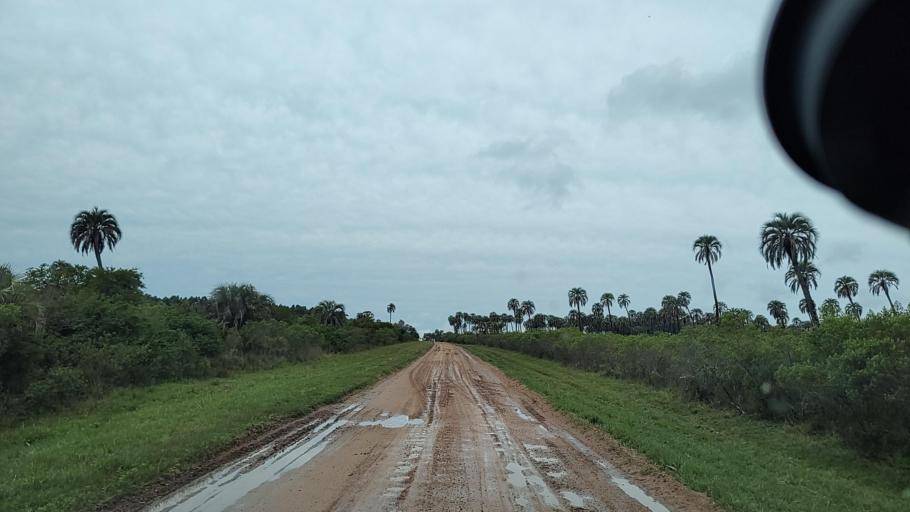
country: AR
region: Entre Rios
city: Ubajay
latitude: -31.8510
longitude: -58.3008
